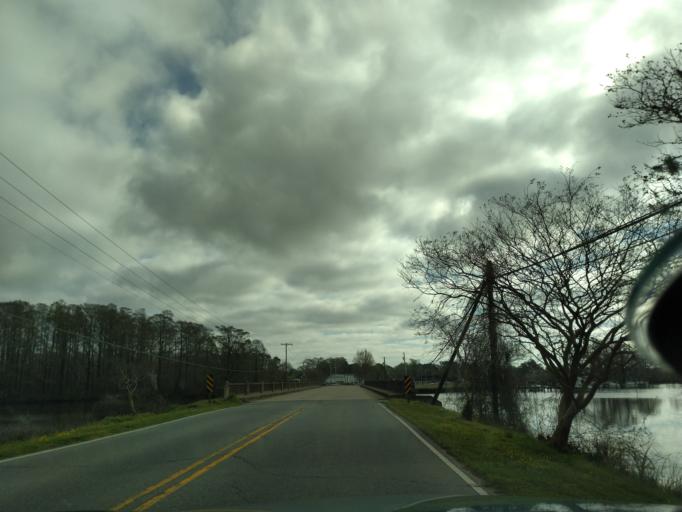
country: US
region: North Carolina
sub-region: Chowan County
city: Edenton
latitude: 36.0576
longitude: -76.6273
